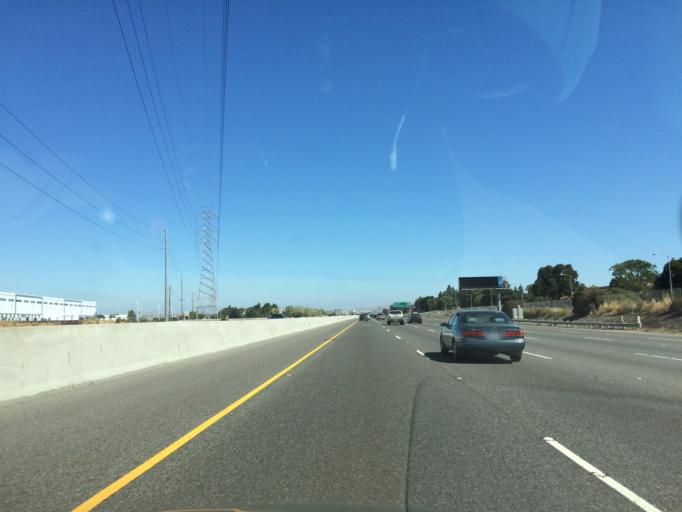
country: US
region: California
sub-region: Santa Clara County
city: Milpitas
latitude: 37.4614
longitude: -121.9252
